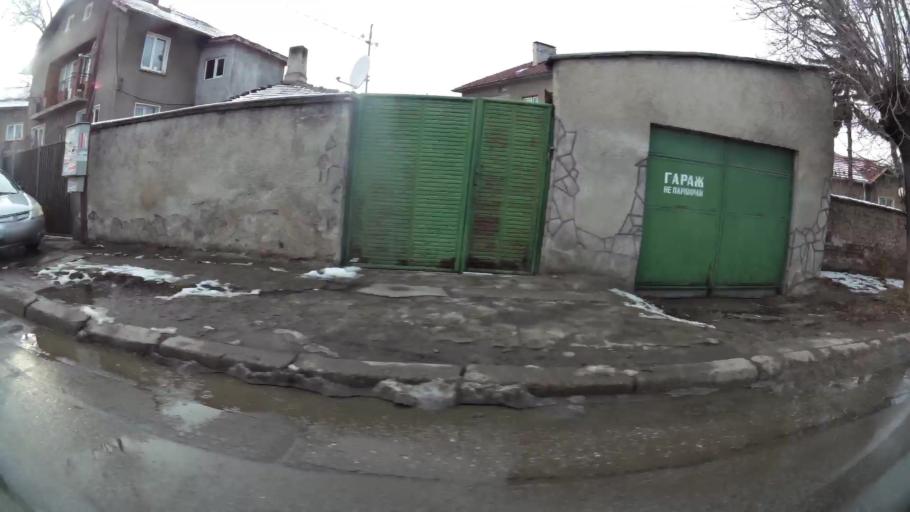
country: BG
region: Sofia-Capital
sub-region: Stolichna Obshtina
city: Sofia
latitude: 42.7164
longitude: 23.3523
